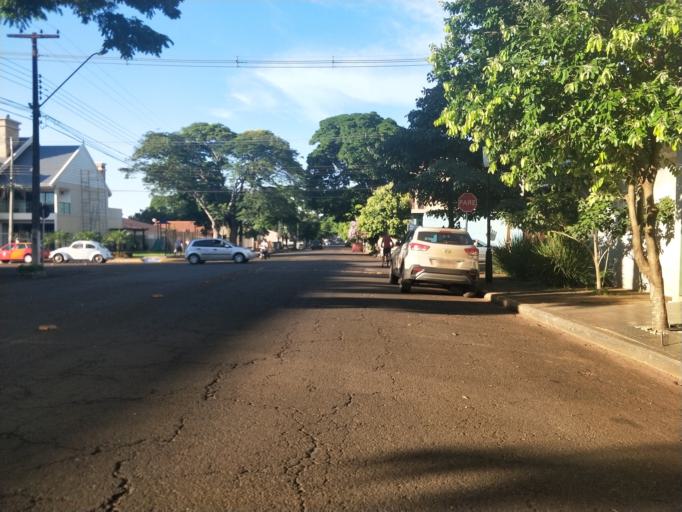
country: BR
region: Parana
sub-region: Marechal Candido Rondon
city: Marechal Candido Rondon
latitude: -24.5555
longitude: -54.0587
